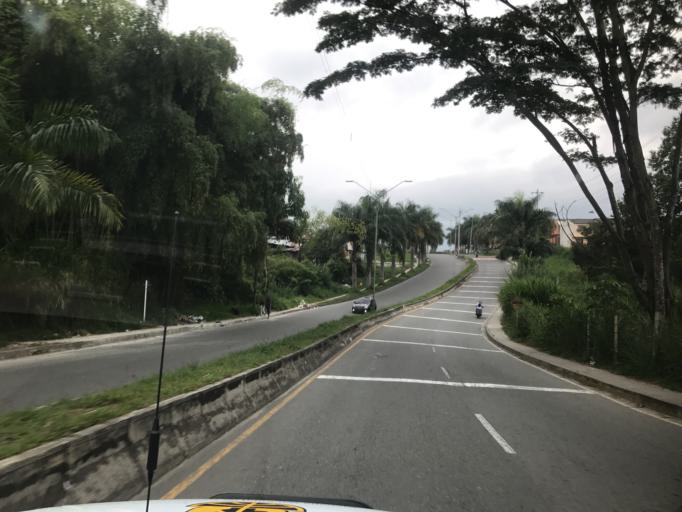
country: CO
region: Quindio
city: Armenia
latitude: 4.5332
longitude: -75.7022
